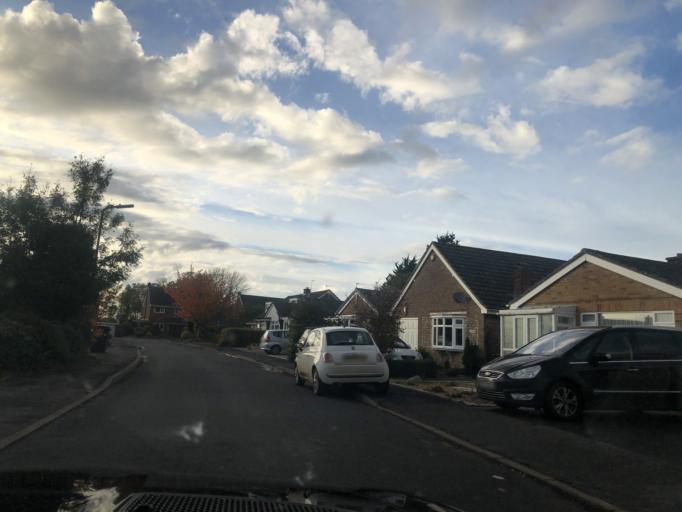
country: GB
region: England
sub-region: Warwickshire
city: Harbury
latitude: 52.2365
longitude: -1.4645
